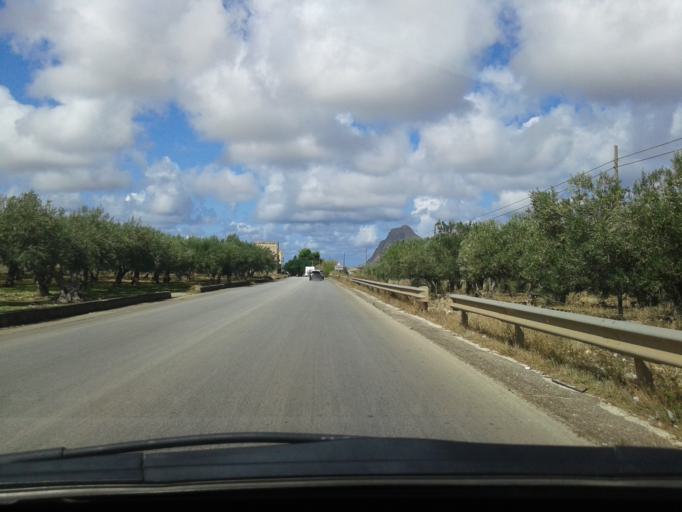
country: IT
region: Sicily
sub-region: Trapani
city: Castelluzzo
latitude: 38.0775
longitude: 12.7276
